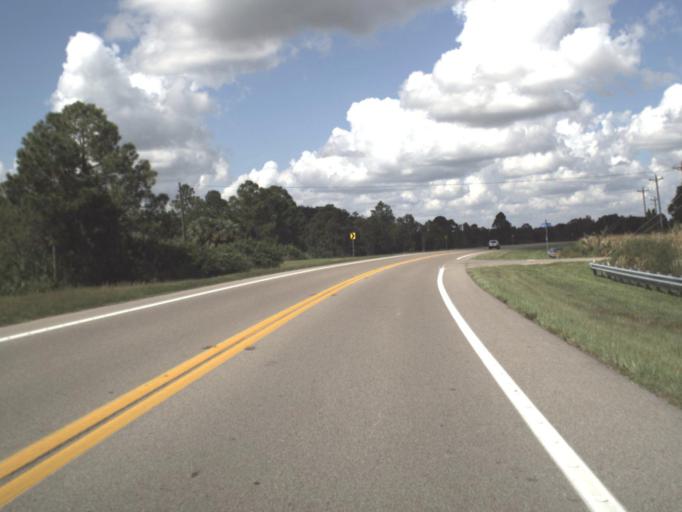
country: US
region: Florida
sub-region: Lee County
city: Lehigh Acres
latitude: 26.5367
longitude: -81.6320
